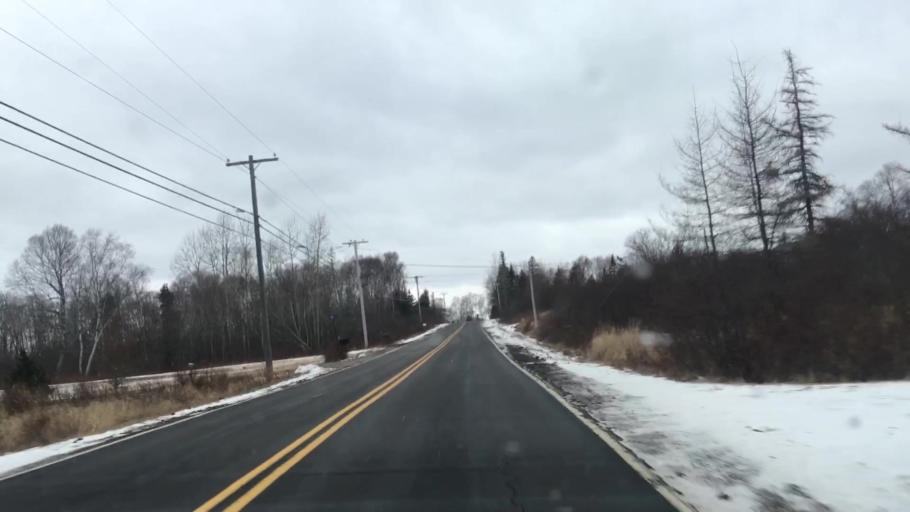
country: US
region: Maine
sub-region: Washington County
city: Machiasport
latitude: 44.7019
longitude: -67.3470
